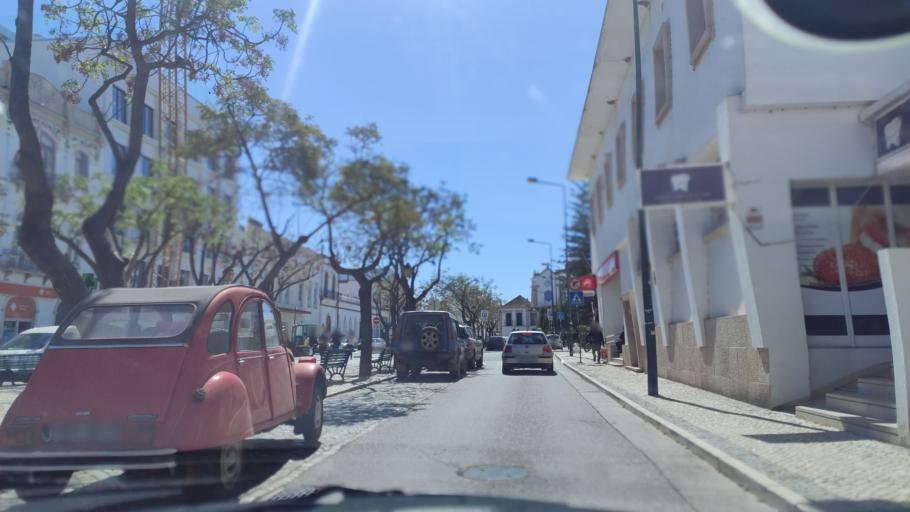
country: PT
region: Faro
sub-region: Olhao
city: Olhao
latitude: 37.0277
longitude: -7.8398
